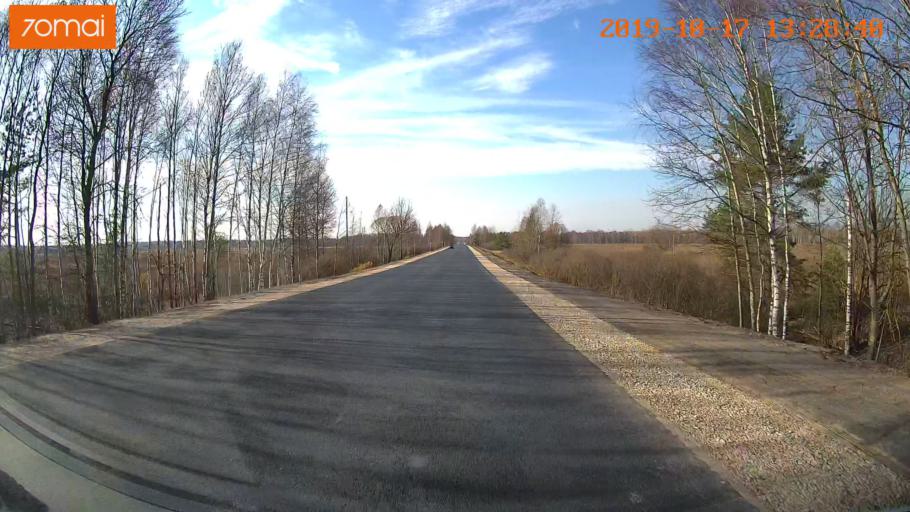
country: RU
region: Vladimir
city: Velikodvorskiy
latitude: 55.1169
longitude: 40.8623
